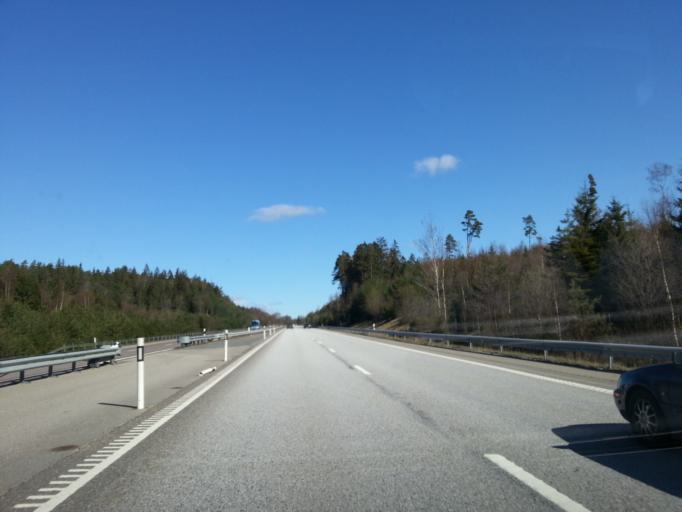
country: SE
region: Vaestra Goetaland
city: Svanesund
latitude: 58.1378
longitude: 11.8855
